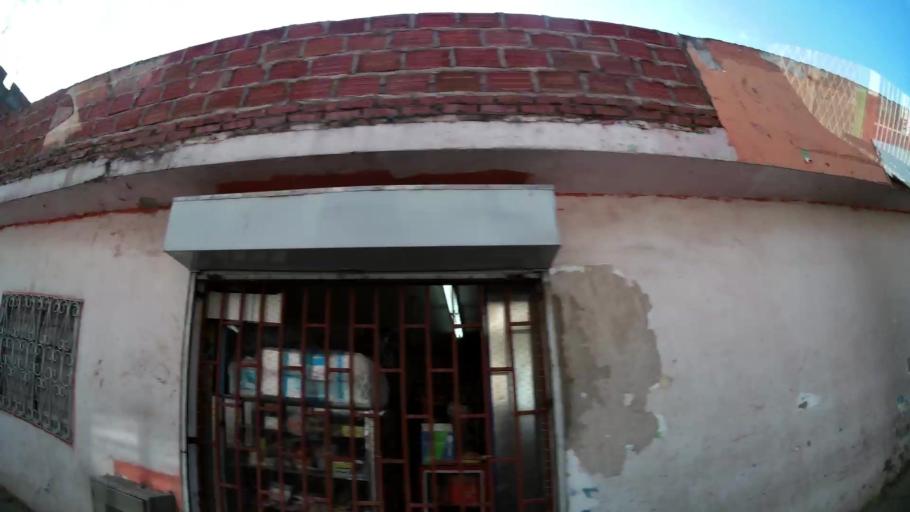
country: CO
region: Valle del Cauca
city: Cali
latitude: 3.4248
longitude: -76.5055
